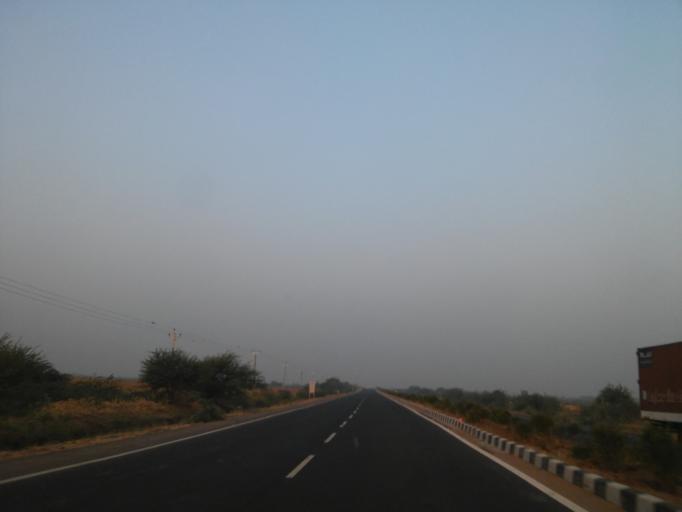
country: IN
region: Gujarat
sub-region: Surendranagar
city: Halvad
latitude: 23.0288
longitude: 70.9609
